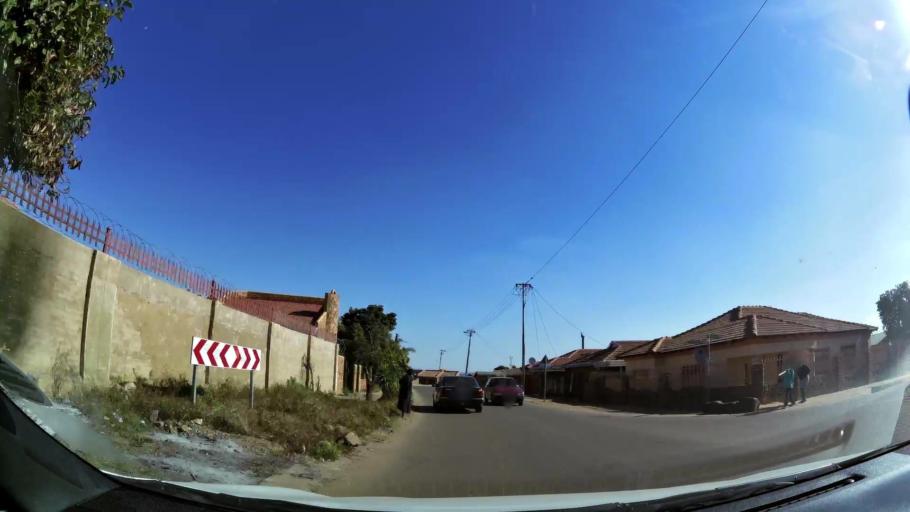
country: ZA
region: Gauteng
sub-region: City of Tshwane Metropolitan Municipality
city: Cullinan
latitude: -25.7138
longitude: 28.3817
